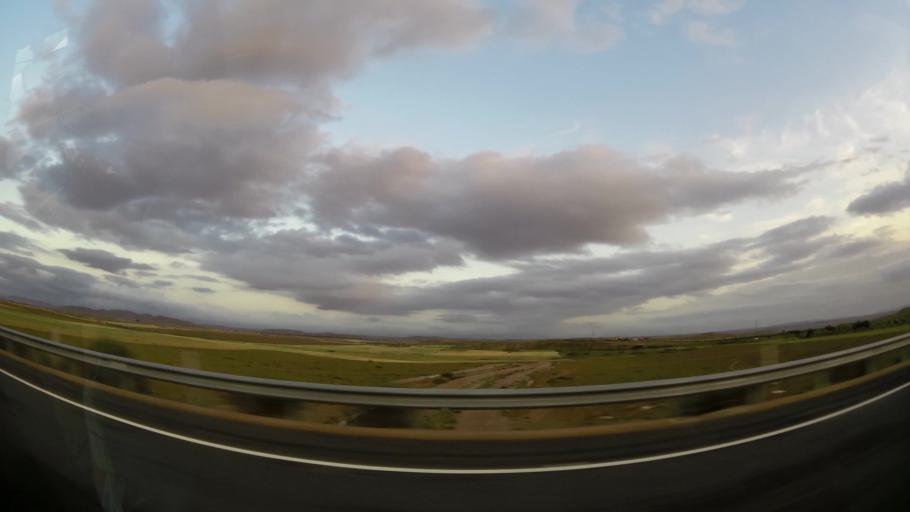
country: MA
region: Oriental
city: Taourirt
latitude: 34.6046
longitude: -2.7627
